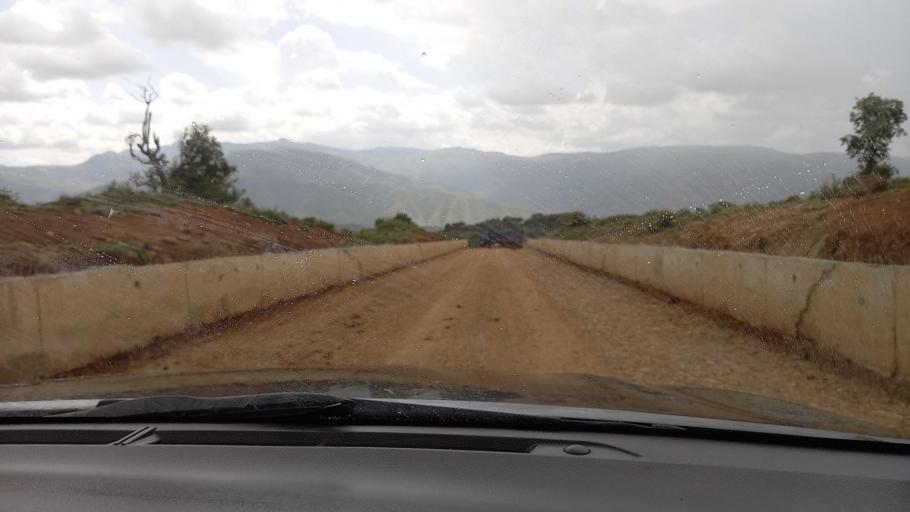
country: ET
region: Southern Nations, Nationalities, and People's Region
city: Mizan Teferi
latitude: 6.1723
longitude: 35.7157
